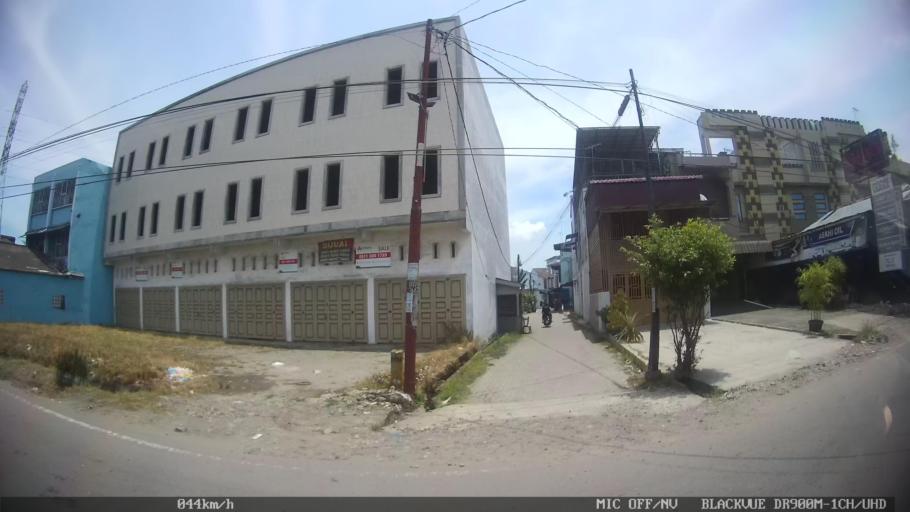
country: ID
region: North Sumatra
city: Labuhan Deli
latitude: 3.7249
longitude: 98.6786
